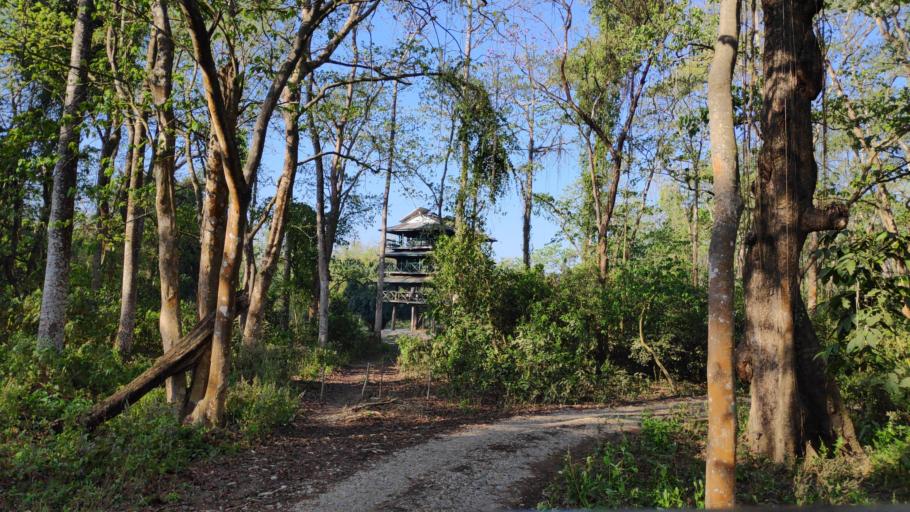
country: NP
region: Central Region
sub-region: Narayani Zone
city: Bharatpur
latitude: 27.5593
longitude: 84.5645
